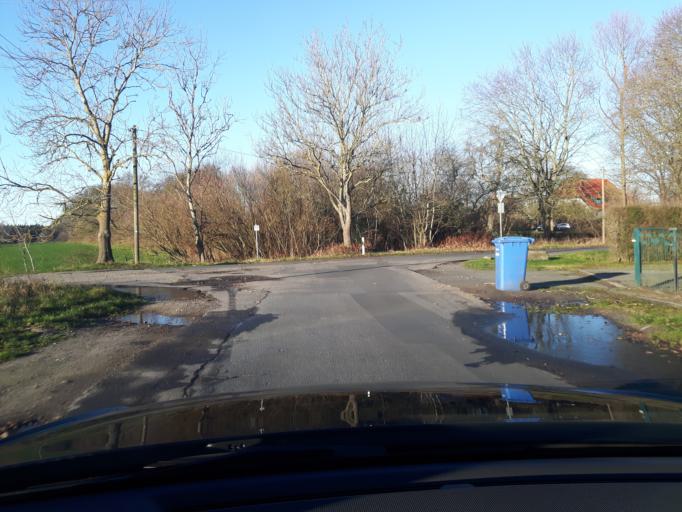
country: DE
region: Mecklenburg-Vorpommern
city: Sehlen
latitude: 54.3628
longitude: 13.4243
